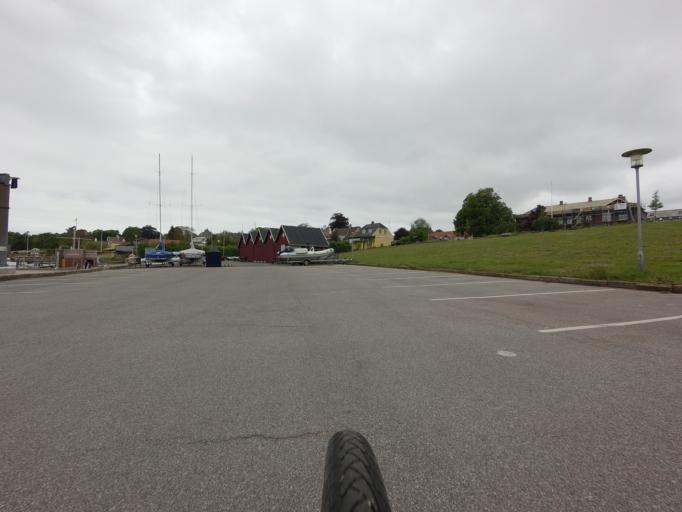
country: DK
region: Zealand
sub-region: Slagelse Kommune
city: Skaelskor
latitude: 55.2527
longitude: 11.2853
